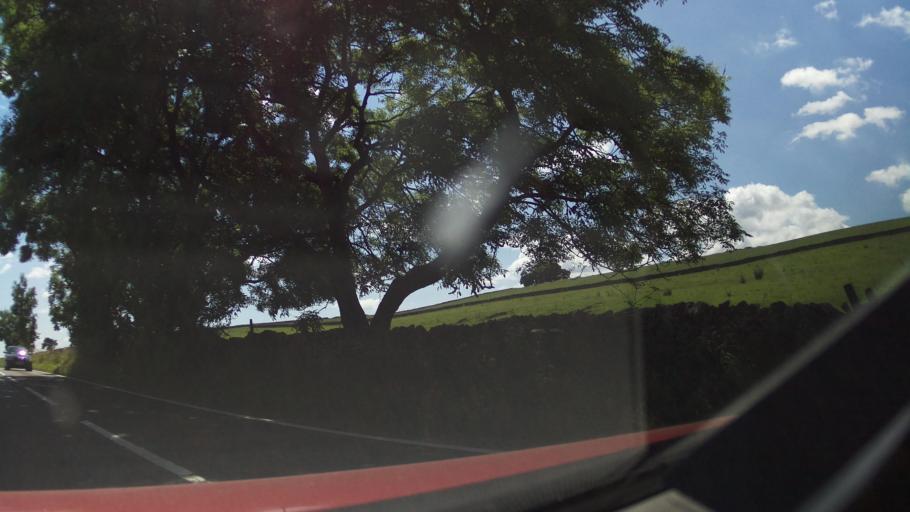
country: GB
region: England
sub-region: Derbyshire
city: Ashbourne
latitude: 53.0765
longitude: -1.7574
